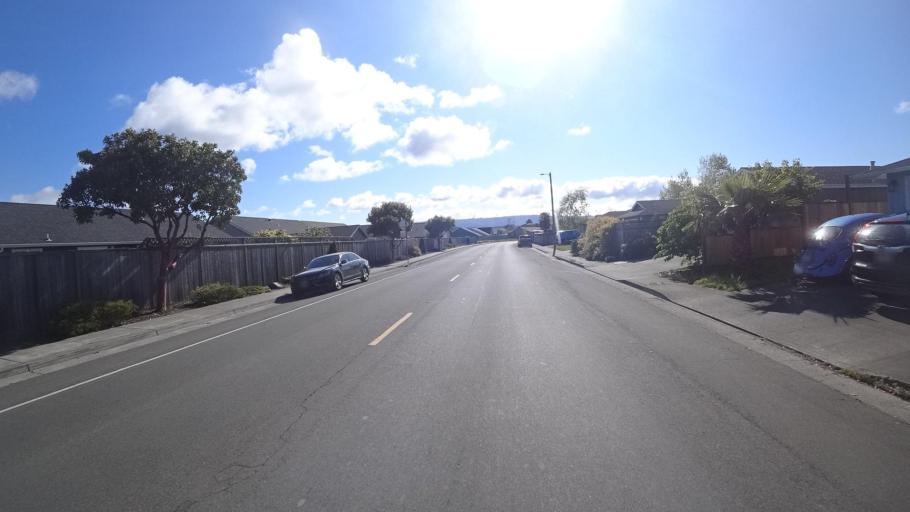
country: US
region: California
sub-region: Humboldt County
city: McKinleyville
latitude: 40.9380
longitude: -124.1101
